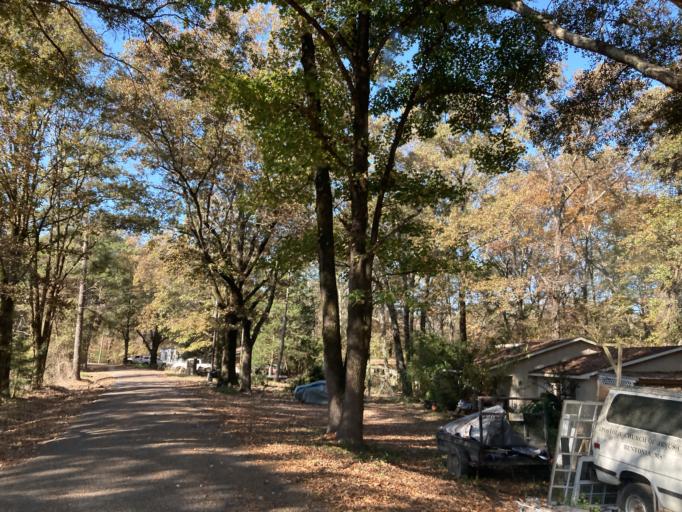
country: US
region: Mississippi
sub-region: Yazoo County
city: Yazoo City
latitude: 32.7460
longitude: -90.3279
